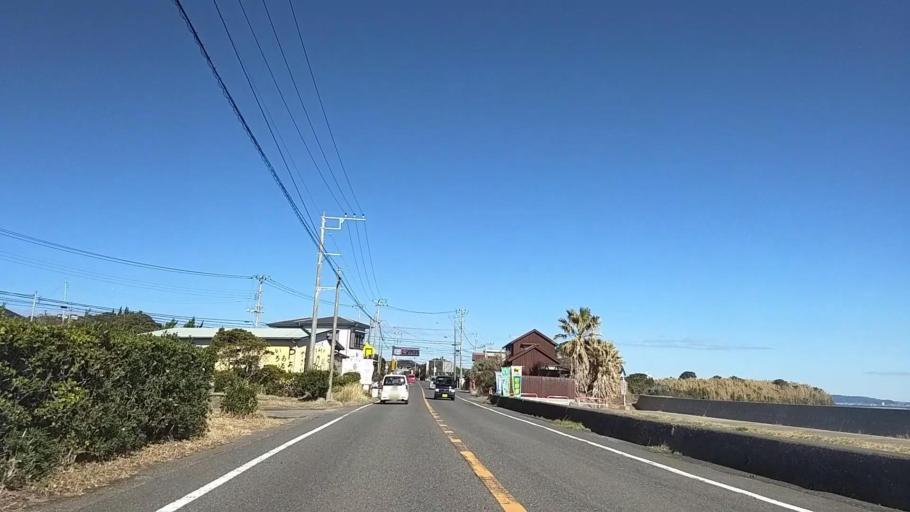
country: JP
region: Chiba
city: Tateyama
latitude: 34.9811
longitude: 139.9668
